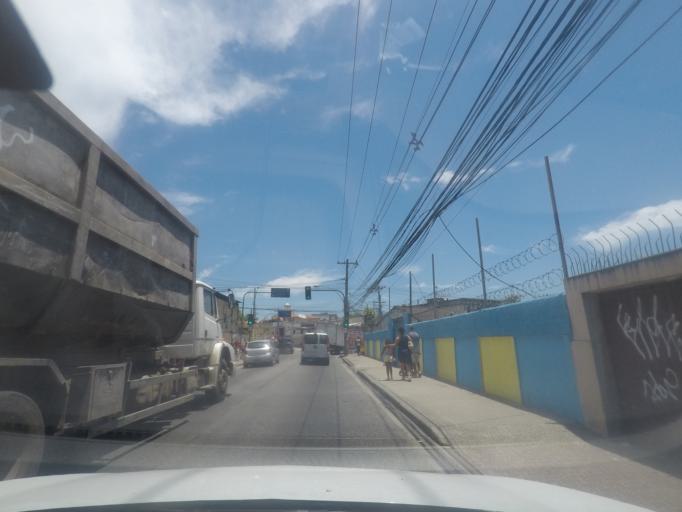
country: BR
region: Rio de Janeiro
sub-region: Itaguai
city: Itaguai
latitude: -22.9141
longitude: -43.6869
